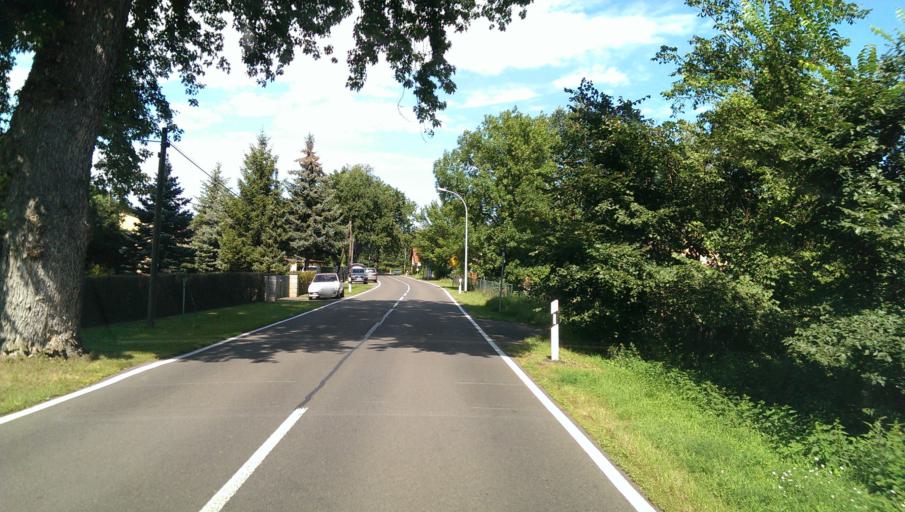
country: DE
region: Brandenburg
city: Trebbin
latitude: 52.2550
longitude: 13.2064
